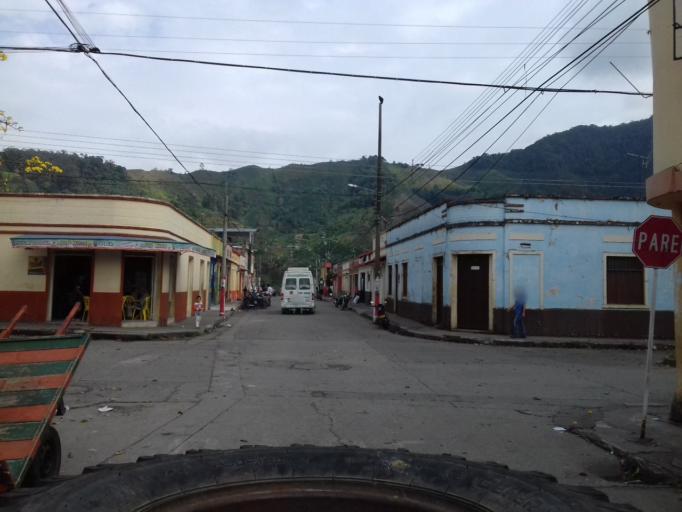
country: CO
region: Tolima
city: Libano
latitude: 4.9256
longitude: -75.0669
